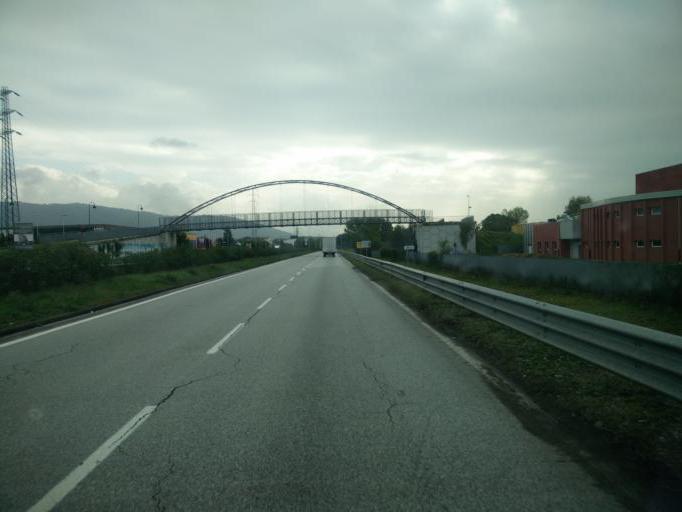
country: IT
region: Tuscany
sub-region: Provincia di Prato
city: Prato
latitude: 43.8772
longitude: 11.0713
